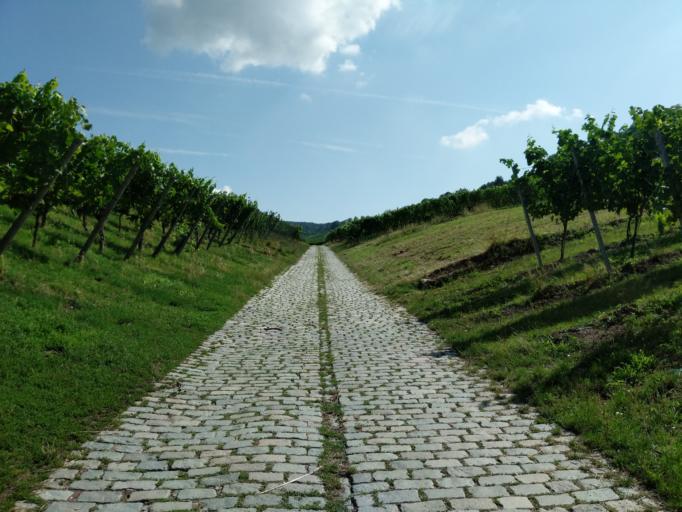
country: DE
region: Baden-Wuerttemberg
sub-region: Regierungsbezirk Stuttgart
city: Fellbach
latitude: 48.7836
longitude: 9.2624
